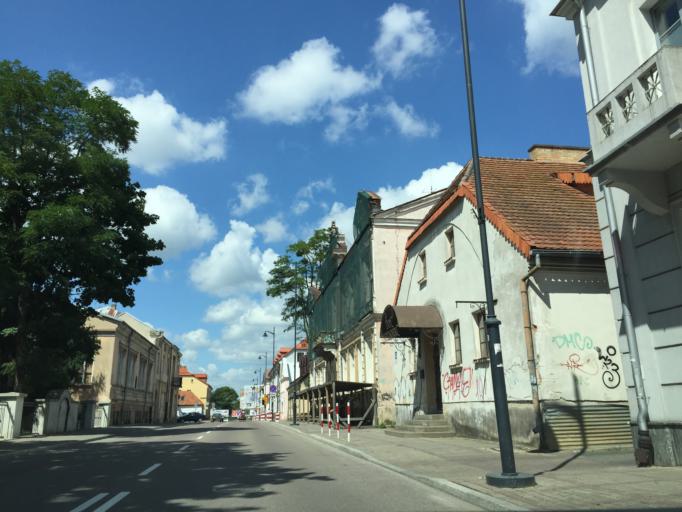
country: PL
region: Podlasie
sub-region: Bialystok
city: Bialystok
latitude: 53.1348
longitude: 23.1680
